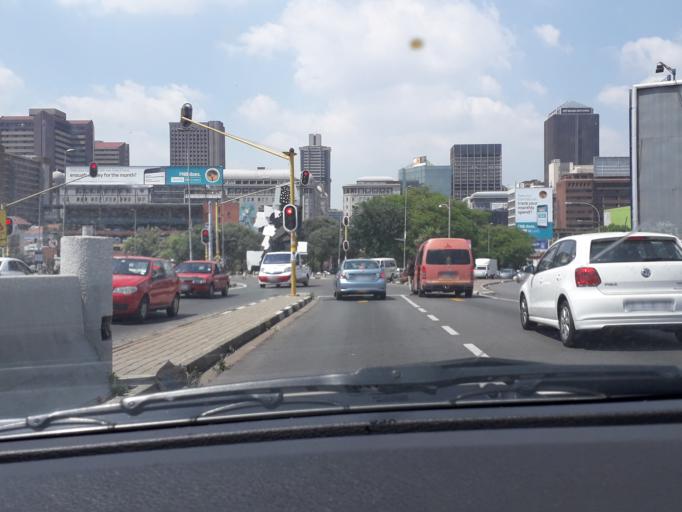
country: ZA
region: Gauteng
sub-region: City of Johannesburg Metropolitan Municipality
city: Johannesburg
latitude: -26.1987
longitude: 28.0377
